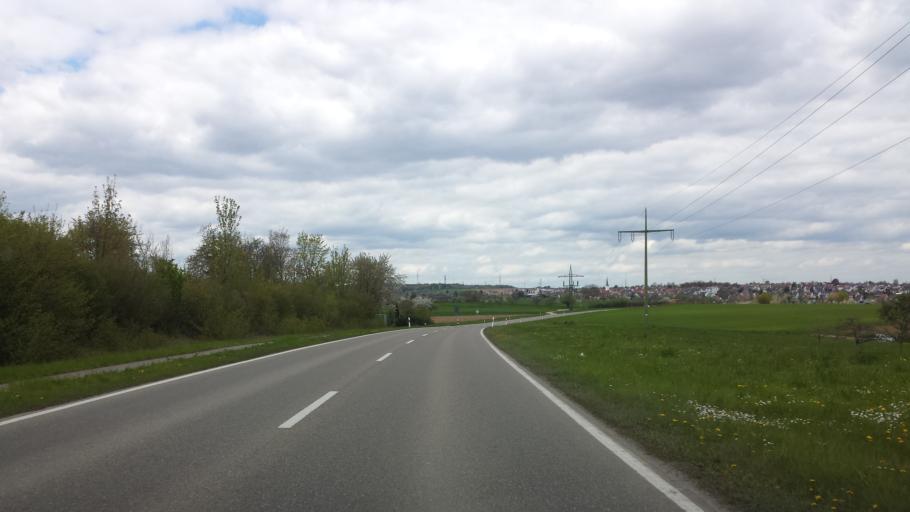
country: DE
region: Baden-Wuerttemberg
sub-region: Regierungsbezirk Stuttgart
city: Leonberg
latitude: 48.8052
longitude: 9.0397
